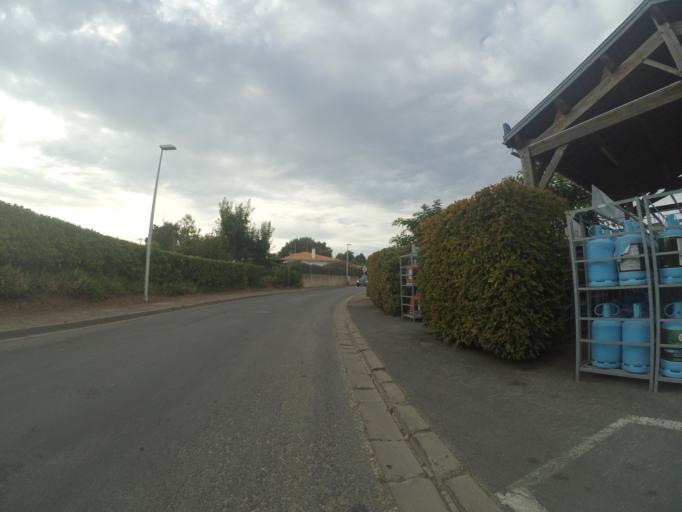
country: FR
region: Poitou-Charentes
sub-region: Departement de la Charente-Maritime
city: Meschers-sur-Gironde
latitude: 45.5586
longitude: -0.9564
